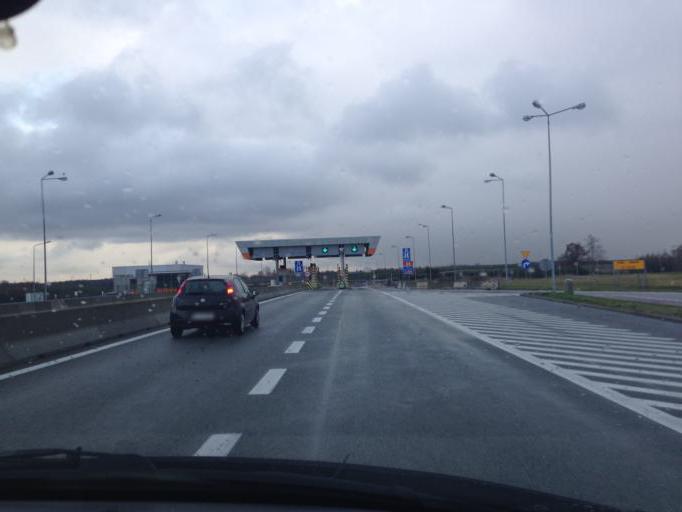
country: PL
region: Opole Voivodeship
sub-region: Powiat strzelecki
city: Ujazd
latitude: 50.4499
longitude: 18.3470
